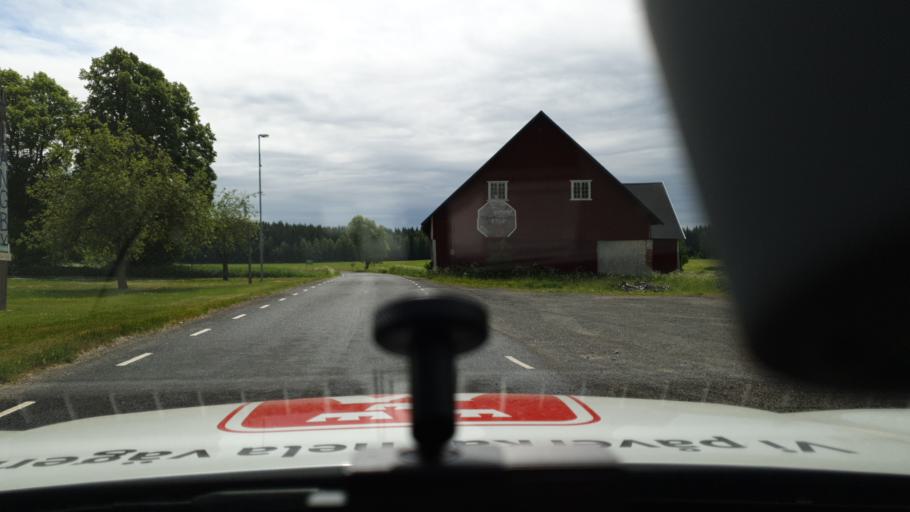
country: SE
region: Joenkoeping
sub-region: Mullsjo Kommun
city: Mullsjoe
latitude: 58.0131
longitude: 13.6935
